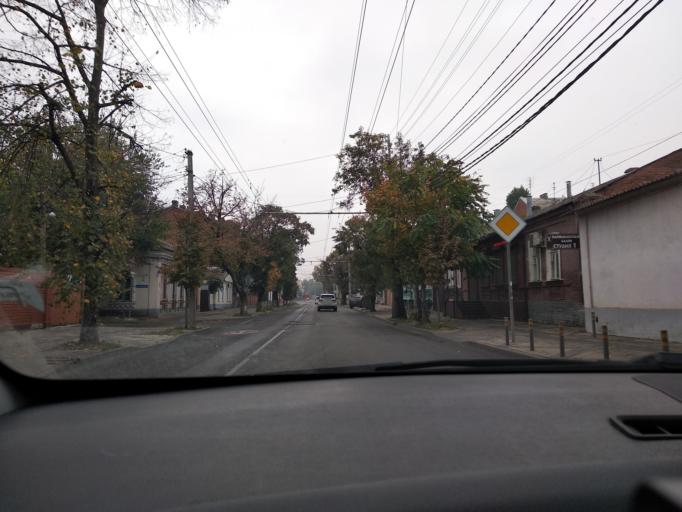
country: RU
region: Krasnodarskiy
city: Krasnodar
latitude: 45.0180
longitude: 38.9750
